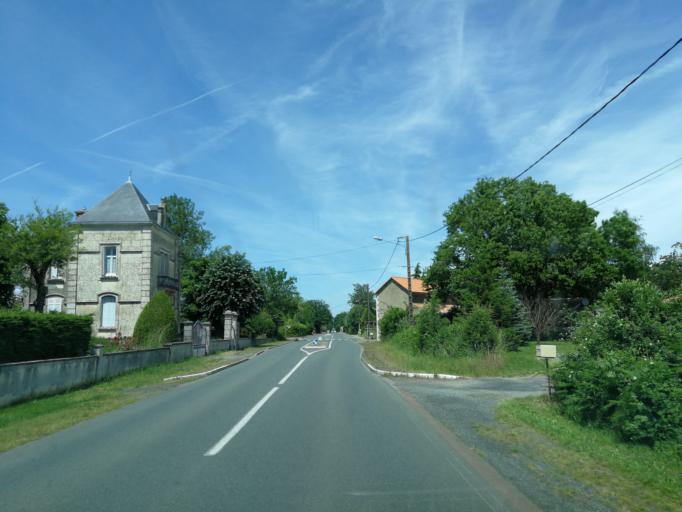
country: FR
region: Pays de la Loire
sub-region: Departement de la Vendee
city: Pissotte
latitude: 46.5288
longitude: -0.8075
